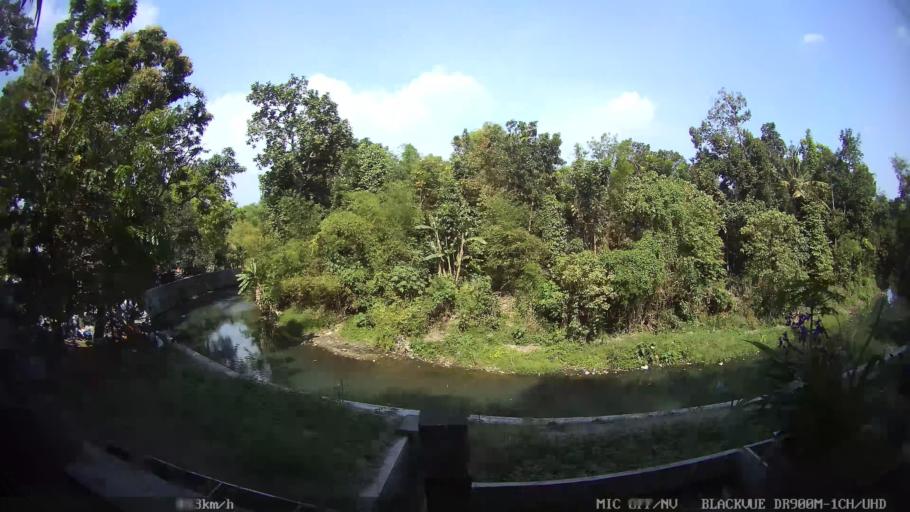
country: ID
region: Daerah Istimewa Yogyakarta
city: Sewon
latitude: -7.8336
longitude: 110.3949
